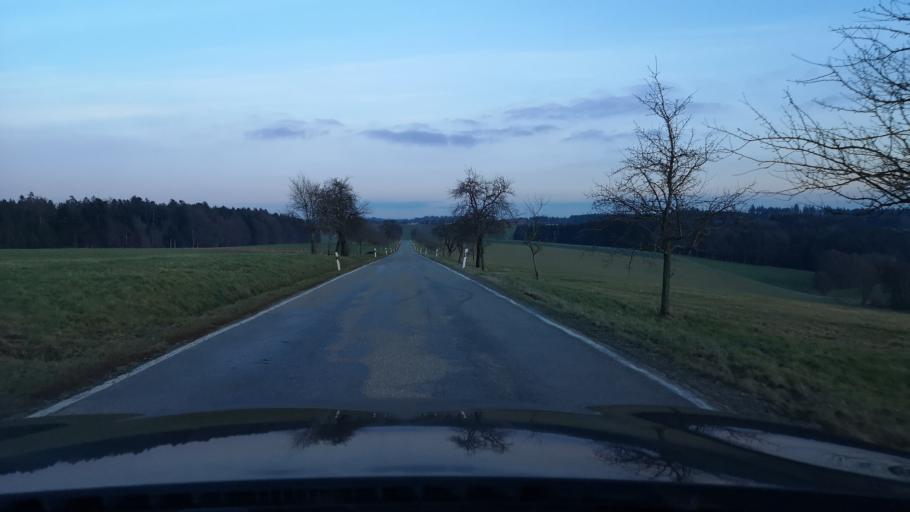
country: DE
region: Baden-Wuerttemberg
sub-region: Regierungsbezirk Stuttgart
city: Kaisersbach
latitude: 48.9358
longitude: 9.6441
